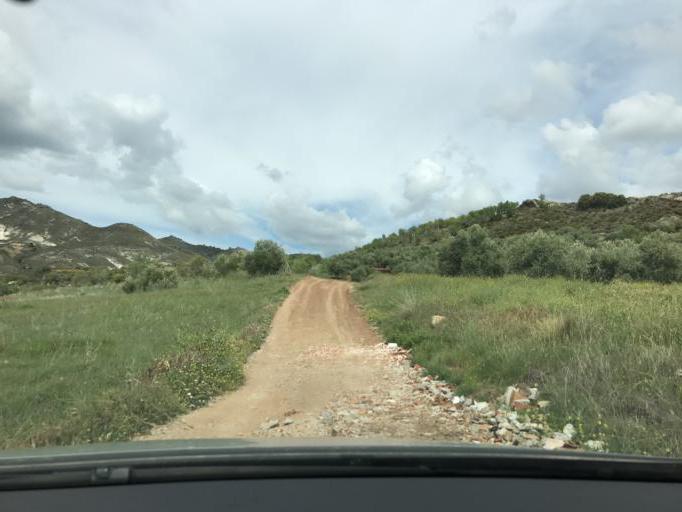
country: ES
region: Andalusia
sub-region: Provincia de Granada
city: Beas de Granada
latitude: 37.2164
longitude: -3.4707
